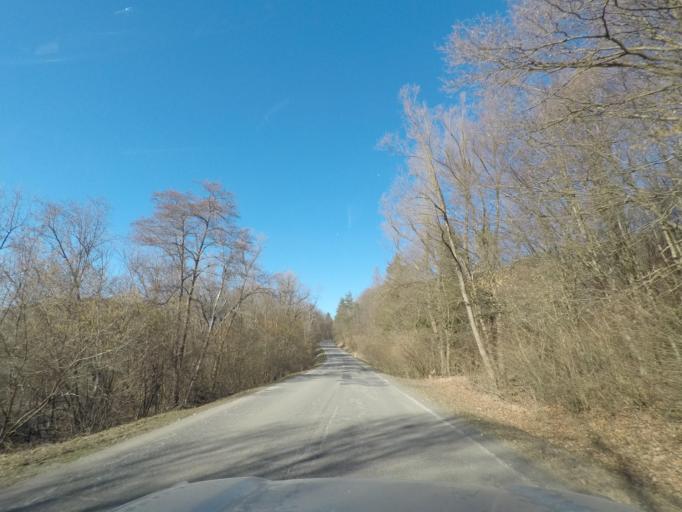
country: SK
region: Presovsky
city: Snina
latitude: 49.0352
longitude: 22.1732
